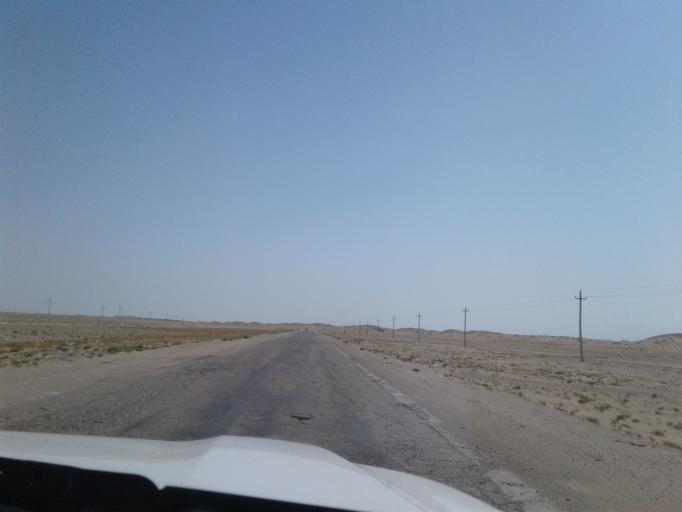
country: TM
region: Balkan
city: Gumdag
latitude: 38.4237
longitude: 54.3926
